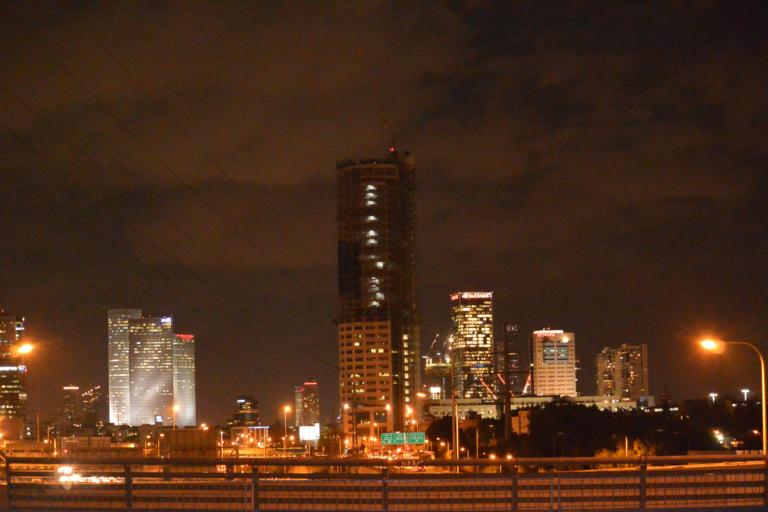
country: IL
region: Tel Aviv
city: Tel Aviv
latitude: 32.0546
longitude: 34.7843
